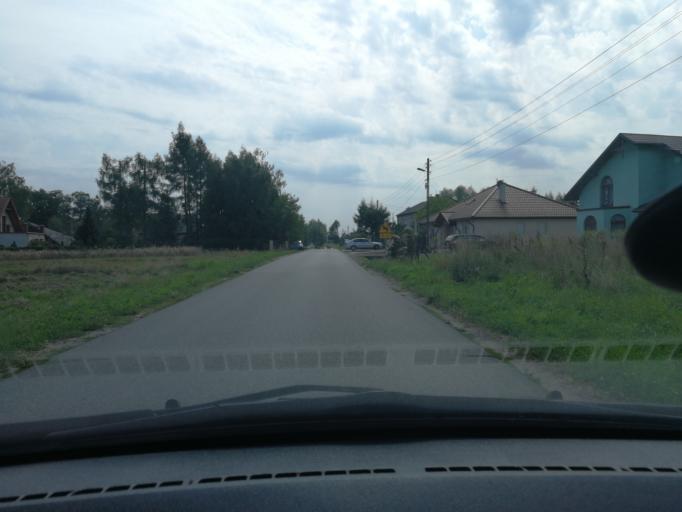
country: PL
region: Lodz Voivodeship
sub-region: Skierniewice
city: Skierniewice
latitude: 51.9781
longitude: 20.1037
